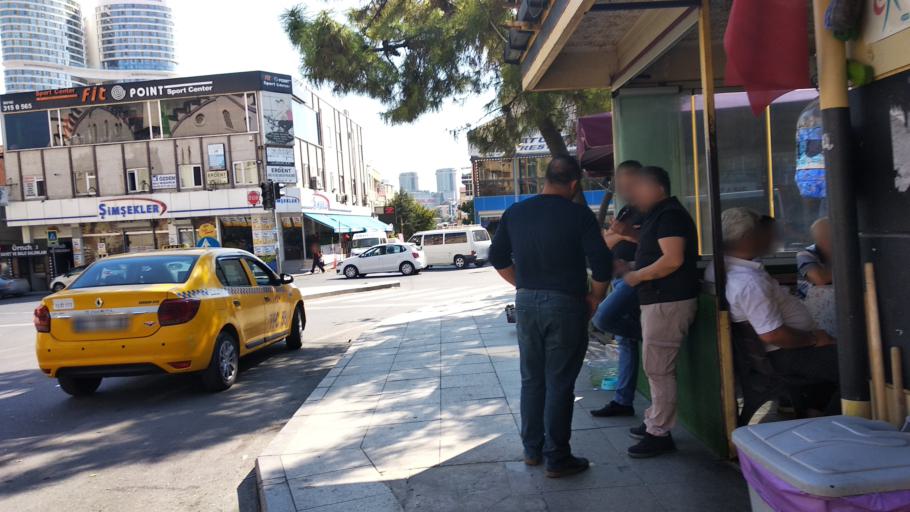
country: TR
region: Istanbul
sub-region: Atasehir
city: Atasehir
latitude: 40.9959
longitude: 29.0829
